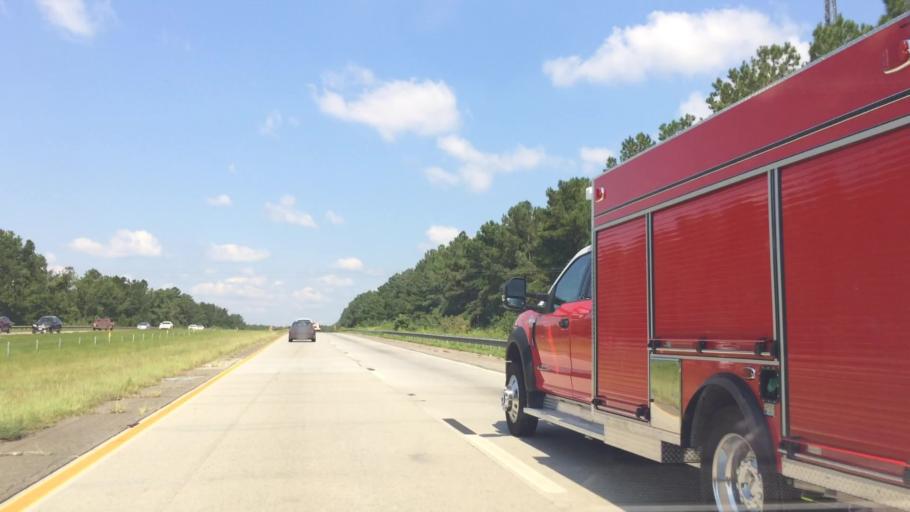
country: US
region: South Carolina
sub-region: Colleton County
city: Walterboro
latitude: 33.0329
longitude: -80.6676
